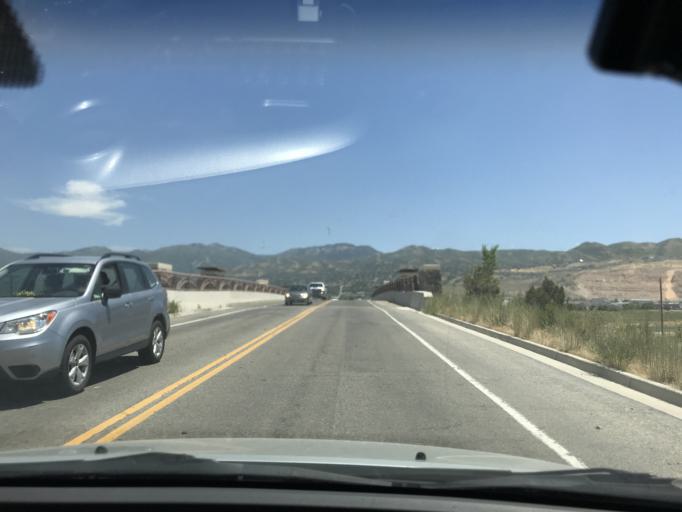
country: US
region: Utah
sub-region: Davis County
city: North Salt Lake
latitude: 40.8415
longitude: -111.9436
